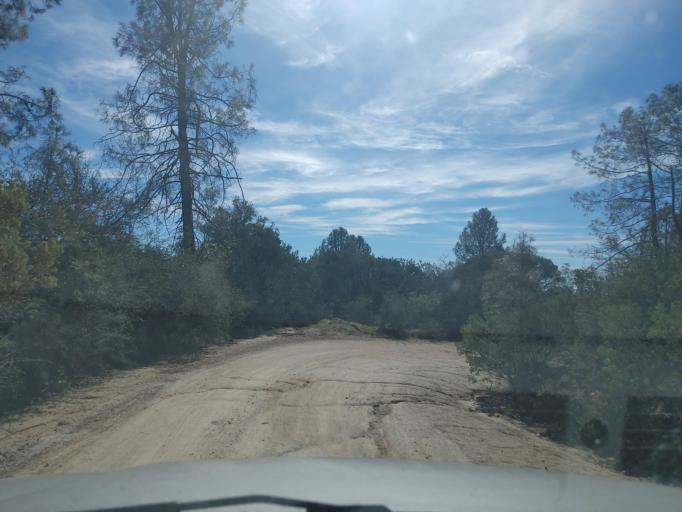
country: US
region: California
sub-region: Madera County
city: Ahwahnee
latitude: 37.4126
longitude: -119.6996
